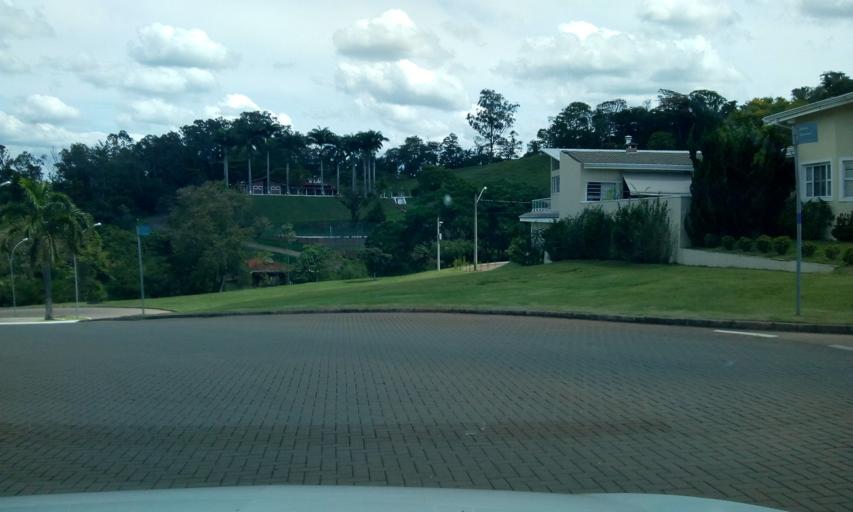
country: BR
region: Sao Paulo
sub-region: Itupeva
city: Itupeva
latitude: -23.1417
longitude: -47.0521
